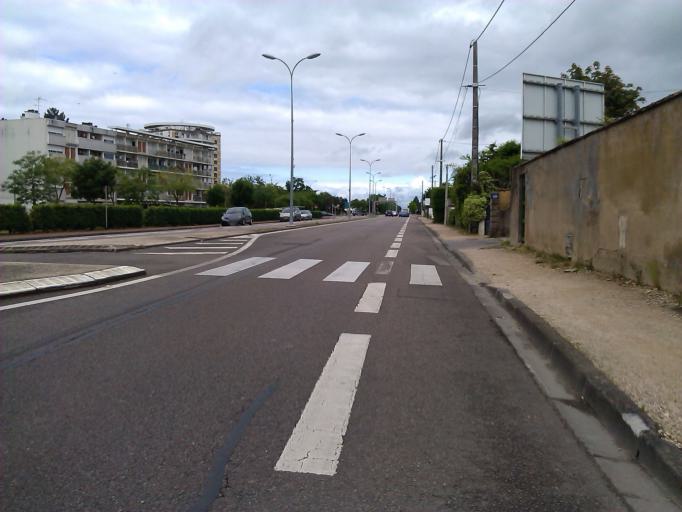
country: FR
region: Bourgogne
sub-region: Departement de Saone-et-Loire
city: Champforgeuil
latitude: 46.8048
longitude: 4.8450
